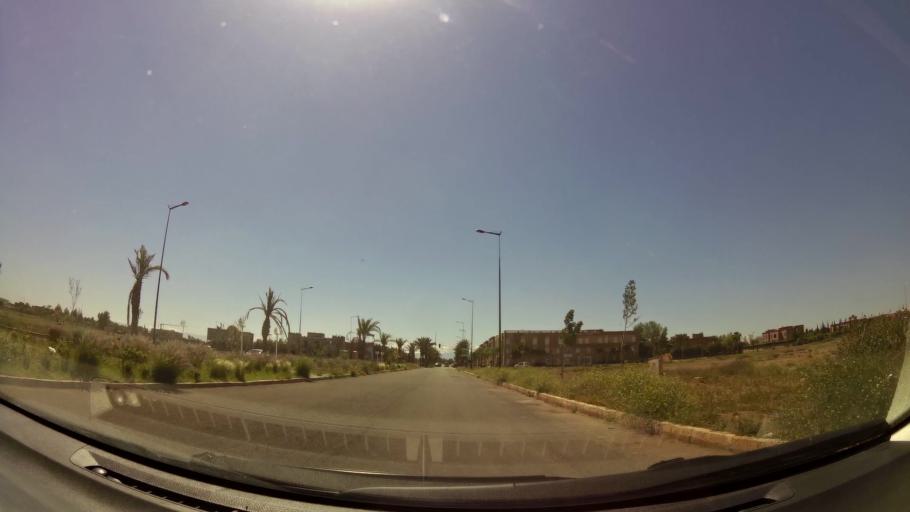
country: MA
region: Marrakech-Tensift-Al Haouz
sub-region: Marrakech
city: Marrakesh
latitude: 31.5919
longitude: -8.0027
